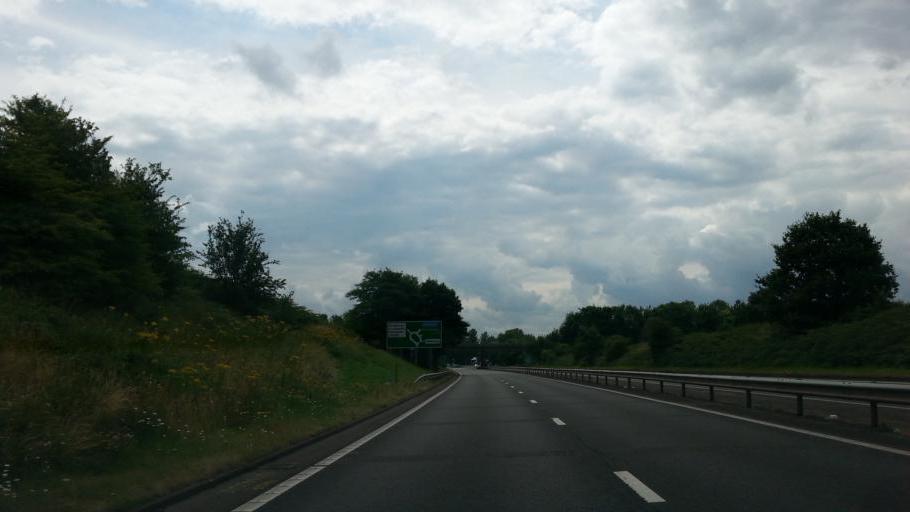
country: GB
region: England
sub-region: Warwickshire
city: Curdworth
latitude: 52.5351
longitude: -1.7777
